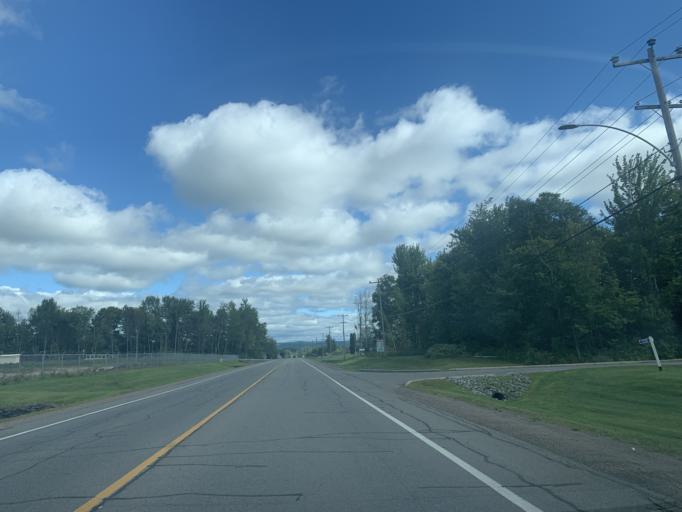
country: CA
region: Ontario
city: Hawkesbury
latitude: 45.5965
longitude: -74.5881
